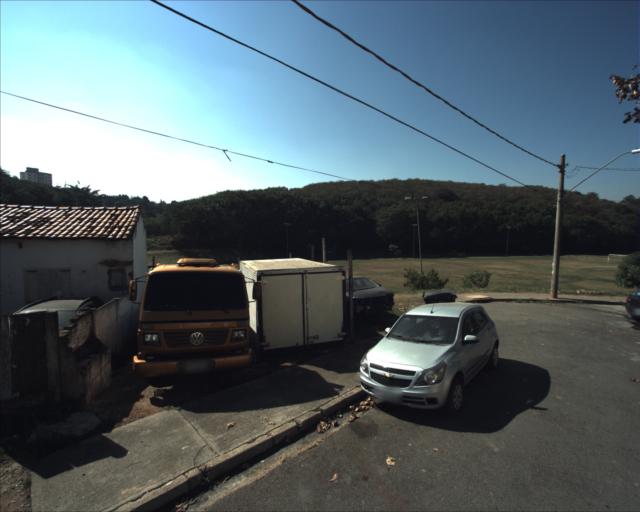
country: BR
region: Sao Paulo
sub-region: Sorocaba
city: Sorocaba
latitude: -23.5035
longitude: -47.4411
